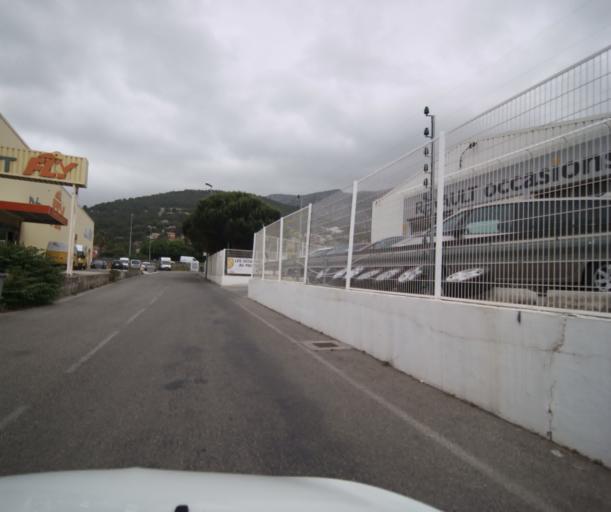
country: FR
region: Provence-Alpes-Cote d'Azur
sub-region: Departement du Var
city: La Valette-du-Var
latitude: 43.1391
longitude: 5.9993
